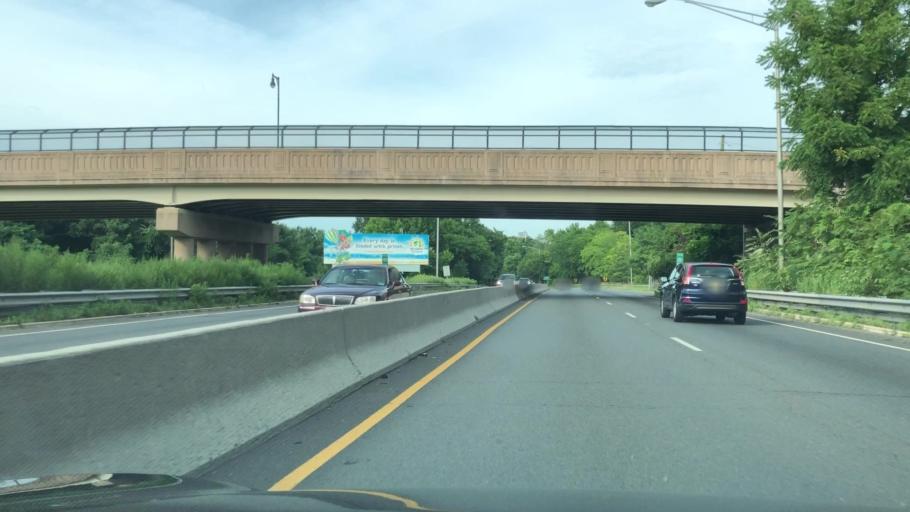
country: US
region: New Jersey
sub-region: Mercer County
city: Prospect Park
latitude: 40.2286
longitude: -74.7566
